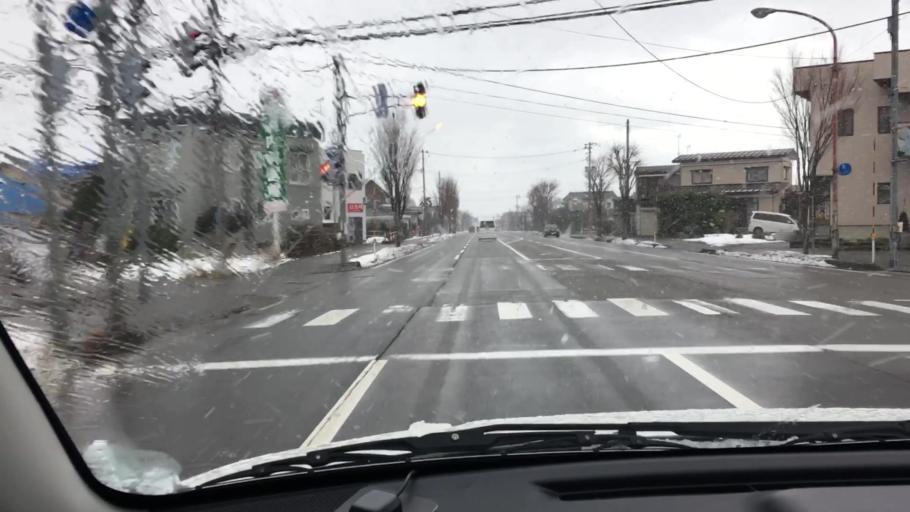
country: JP
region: Niigata
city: Joetsu
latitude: 37.1175
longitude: 138.2329
